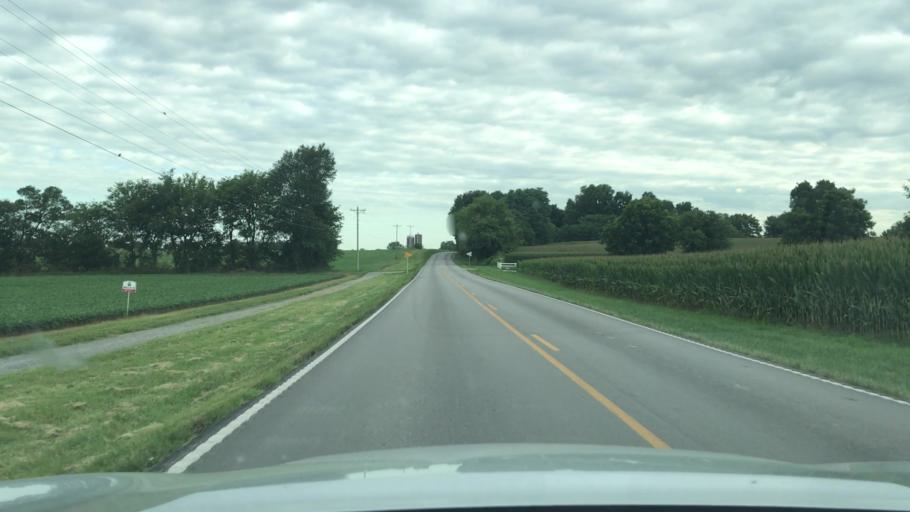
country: US
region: Kentucky
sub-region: Todd County
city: Guthrie
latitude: 36.6888
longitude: -87.2011
